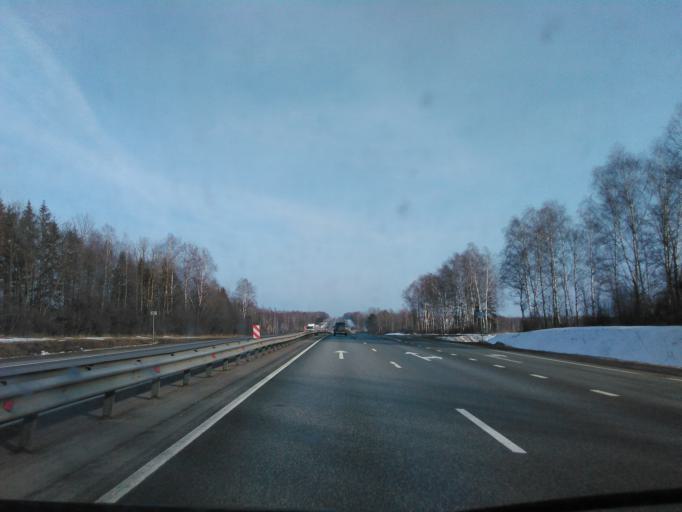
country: RU
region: Smolensk
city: Verkhnedneprovskiy
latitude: 55.1824
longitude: 33.5283
